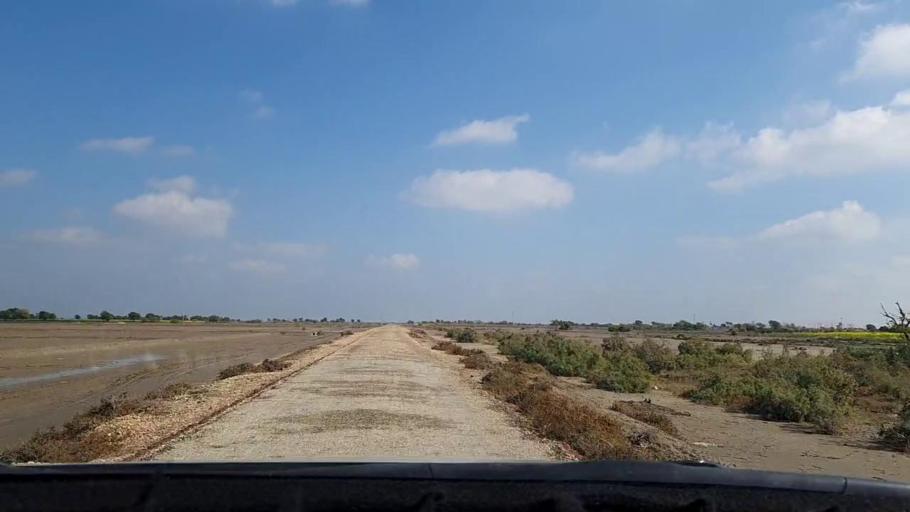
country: PK
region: Sindh
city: Pithoro
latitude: 25.7370
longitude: 69.2643
